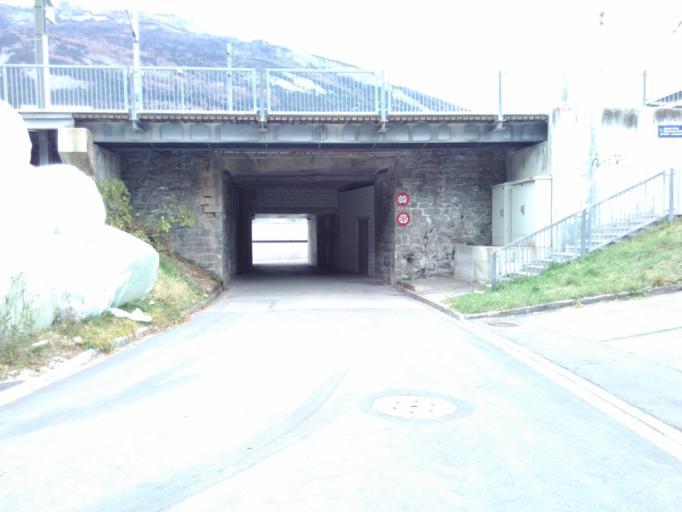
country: CH
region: Grisons
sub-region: Plessur District
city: Chur
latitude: 46.8499
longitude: 9.5129
